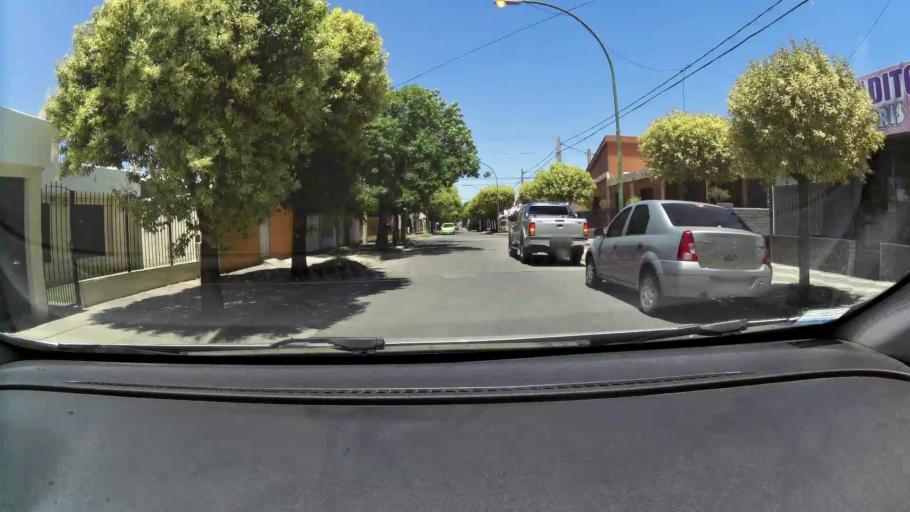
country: AR
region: Cordoba
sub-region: Departamento de Capital
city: Cordoba
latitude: -31.3802
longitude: -64.1372
